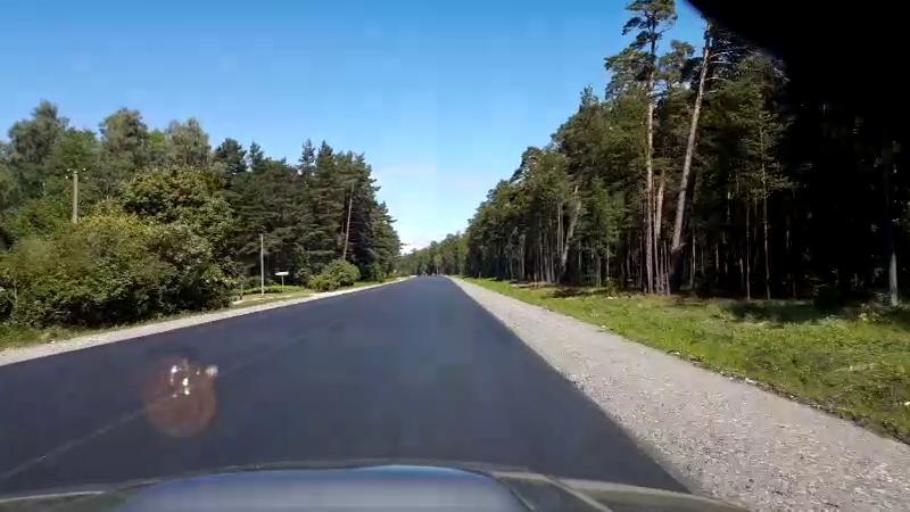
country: LV
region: Salacgrivas
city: Ainazi
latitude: 57.8189
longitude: 24.3471
